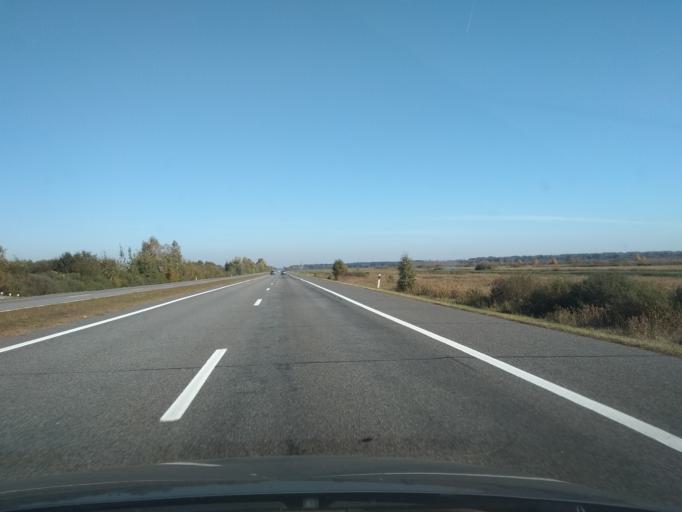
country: BY
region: Brest
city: Byaroza
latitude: 52.5018
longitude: 24.9942
